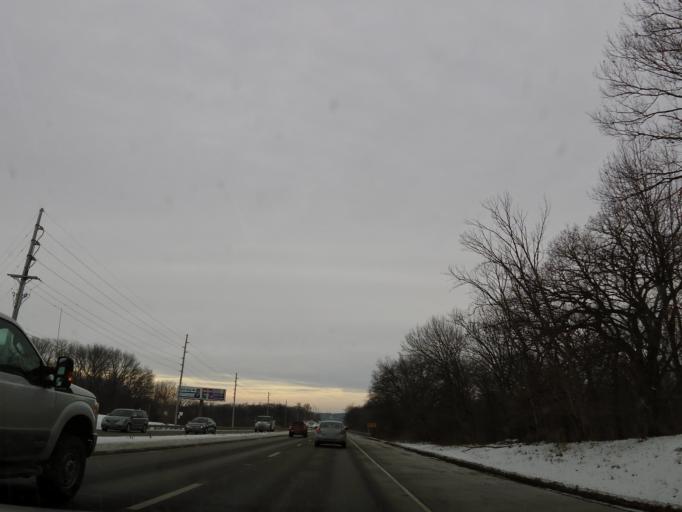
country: US
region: Illinois
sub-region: LaSalle County
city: Peru
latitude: 41.3372
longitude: -89.1202
